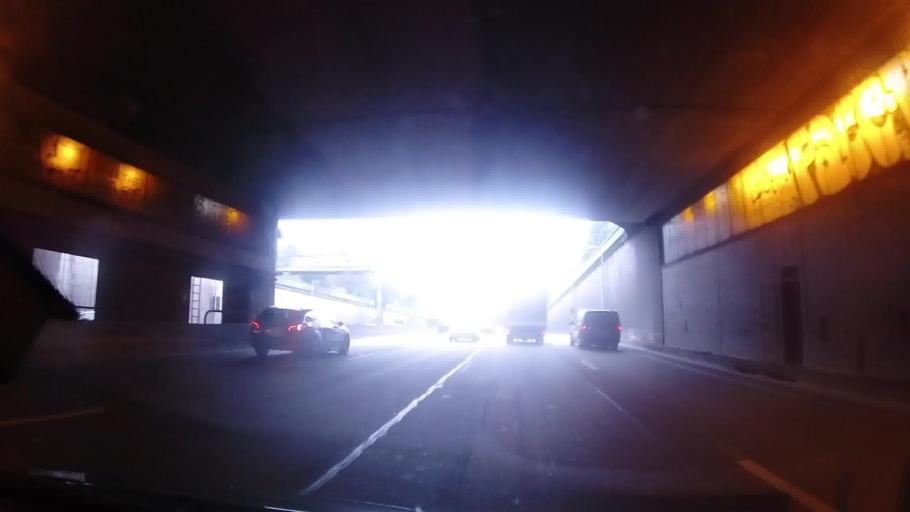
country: FR
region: Ile-de-France
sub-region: Departement des Hauts-de-Seine
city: Boulogne-Billancourt
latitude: 48.8552
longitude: 2.2523
